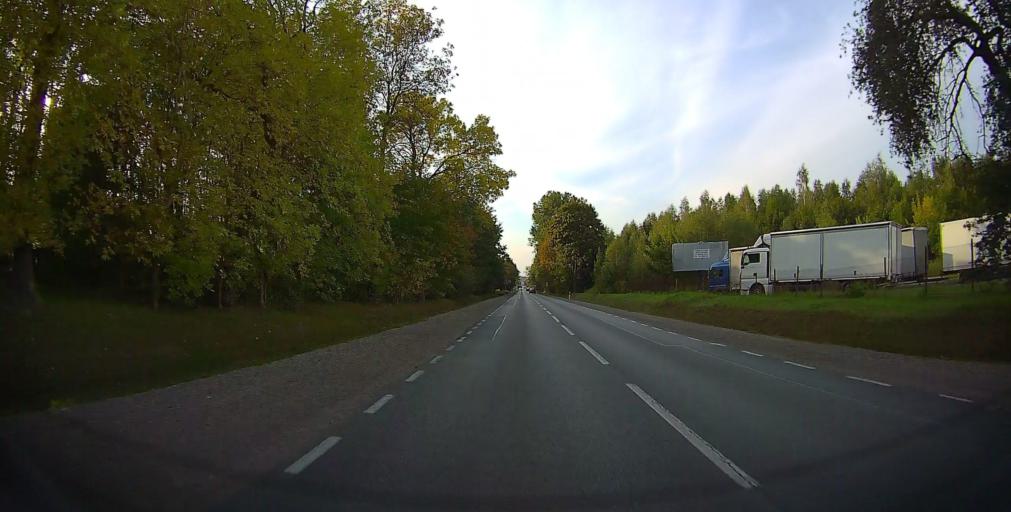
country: PL
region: Masovian Voivodeship
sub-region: Powiat piaseczynski
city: Zabieniec
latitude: 52.0558
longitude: 21.0537
